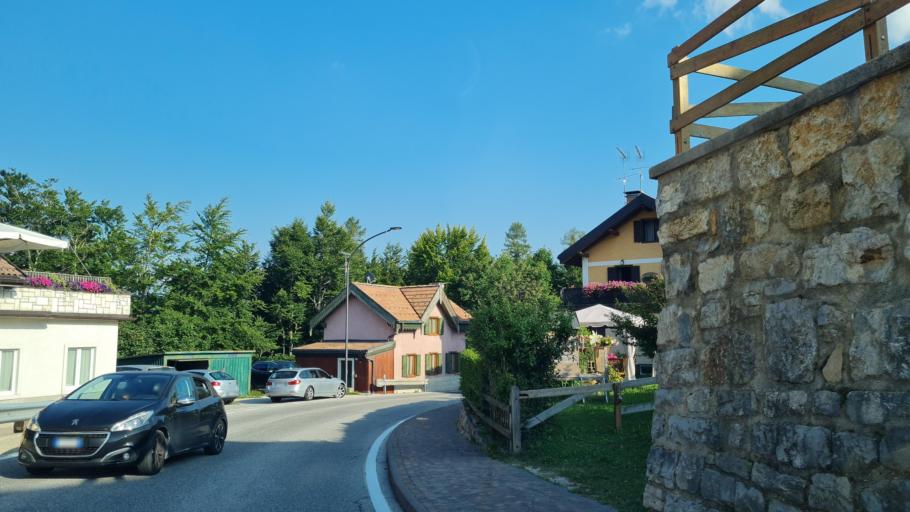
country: IT
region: Trentino-Alto Adige
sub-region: Provincia di Trento
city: Gionghi-Cappella
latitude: 45.9401
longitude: 11.2540
